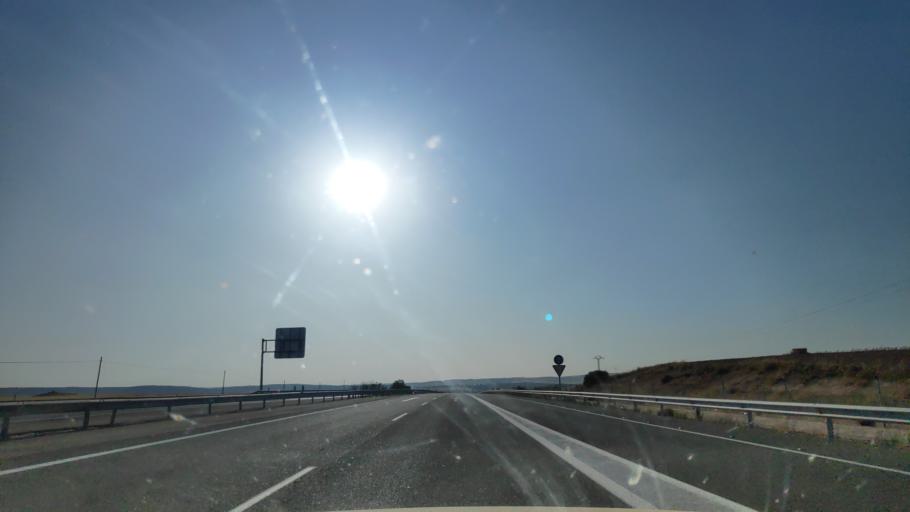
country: ES
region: Castille-La Mancha
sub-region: Provincia de Cuenca
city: Montalbo
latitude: 39.8881
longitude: -2.6863
